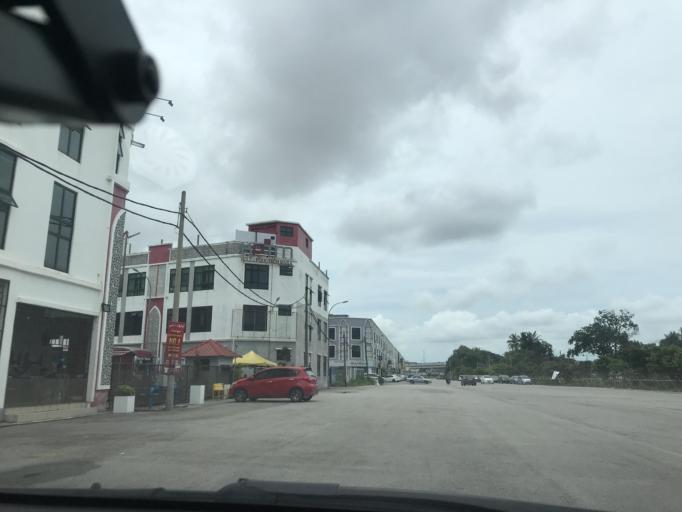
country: MY
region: Kelantan
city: Kota Bharu
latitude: 6.1116
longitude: 102.2329
